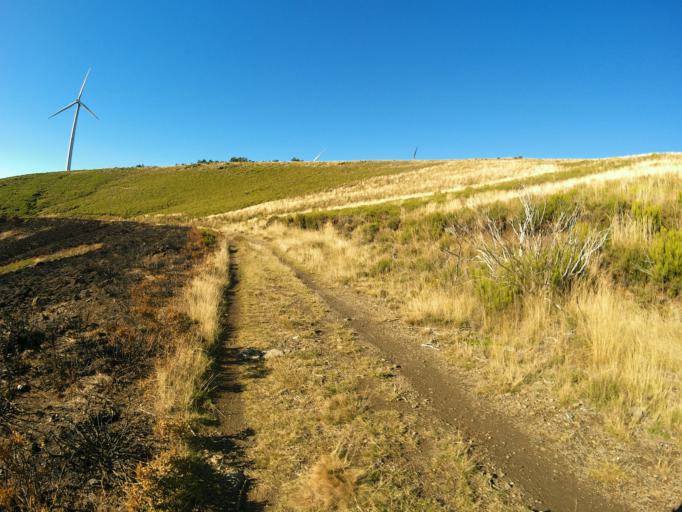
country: PT
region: Vila Real
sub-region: Mesao Frio
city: Mesao Frio
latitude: 41.2373
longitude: -7.9039
